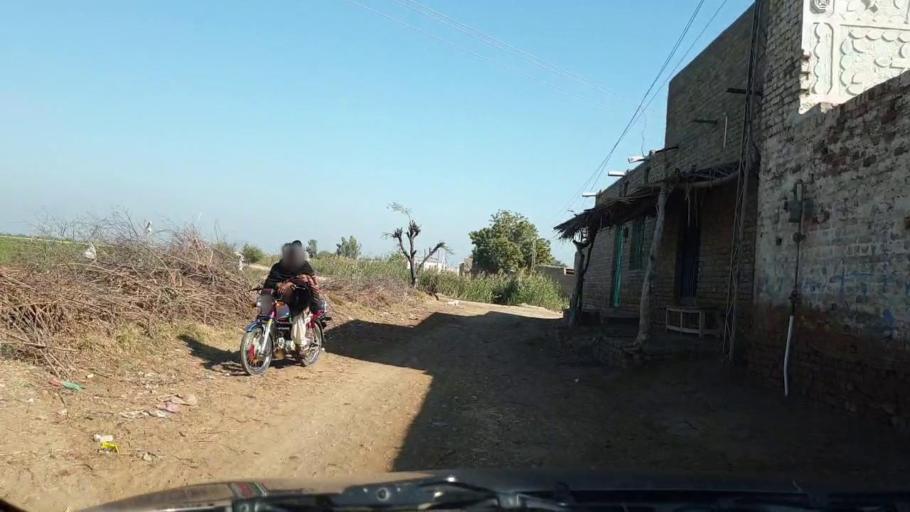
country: PK
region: Sindh
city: Sinjhoro
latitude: 25.9632
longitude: 68.7513
